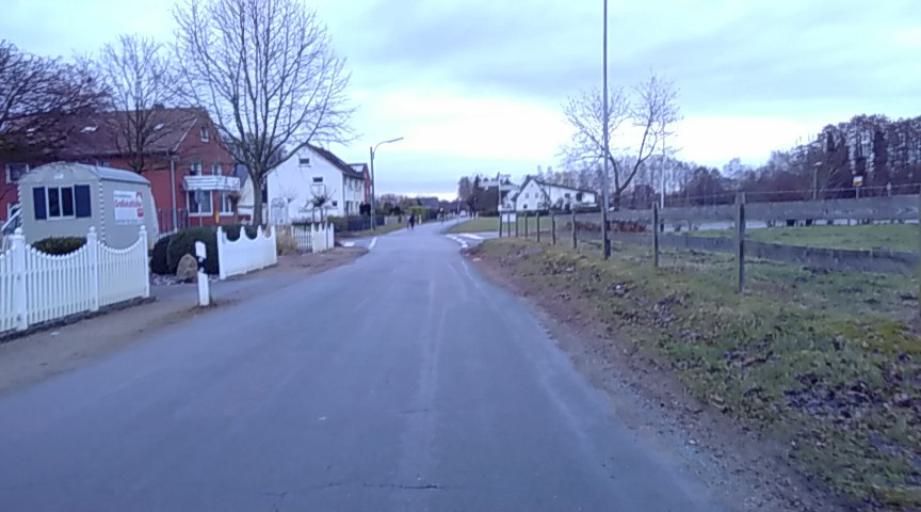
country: DE
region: North Rhine-Westphalia
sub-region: Regierungsbezirk Detmold
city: Verl
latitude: 51.8885
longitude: 8.4711
